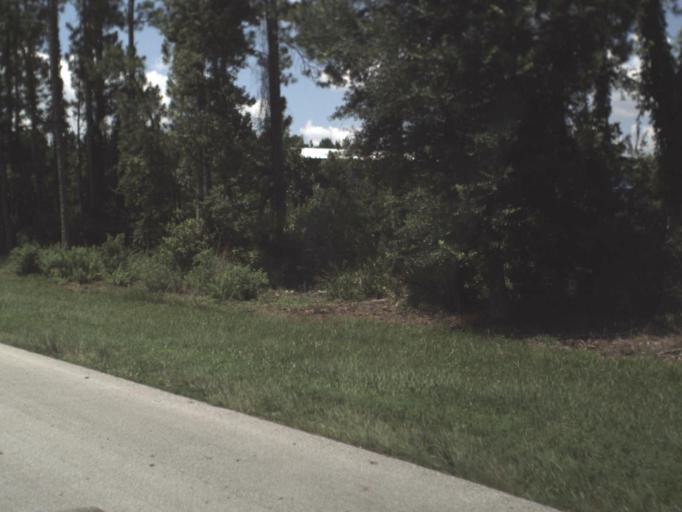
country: US
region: Florida
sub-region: Saint Johns County
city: Saint Augustine South
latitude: 29.8349
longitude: -81.3840
